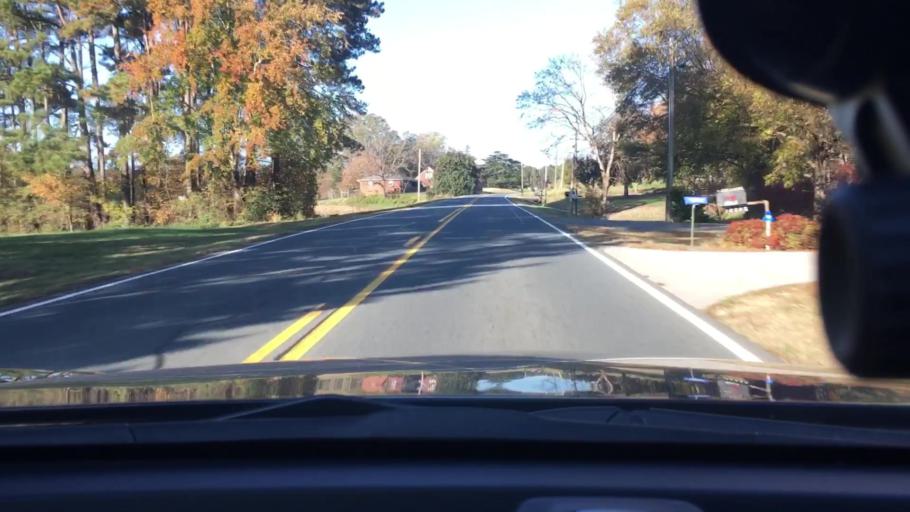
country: US
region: North Carolina
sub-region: Cabarrus County
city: Mount Pleasant
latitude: 35.3833
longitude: -80.3518
